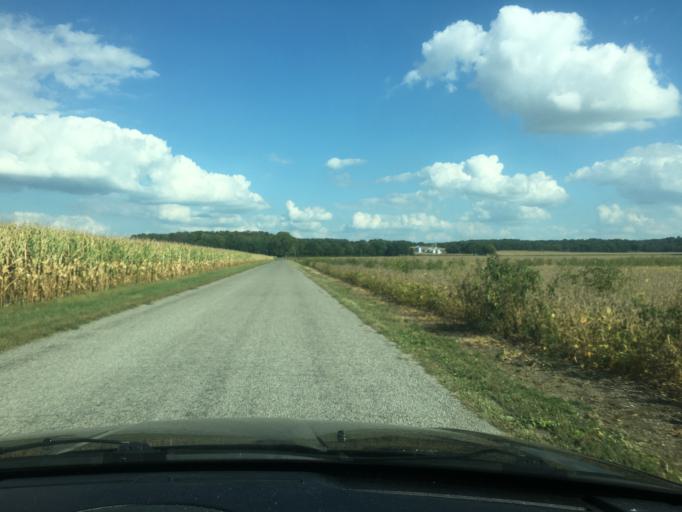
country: US
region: Ohio
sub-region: Logan County
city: West Liberty
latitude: 40.2451
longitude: -83.7362
